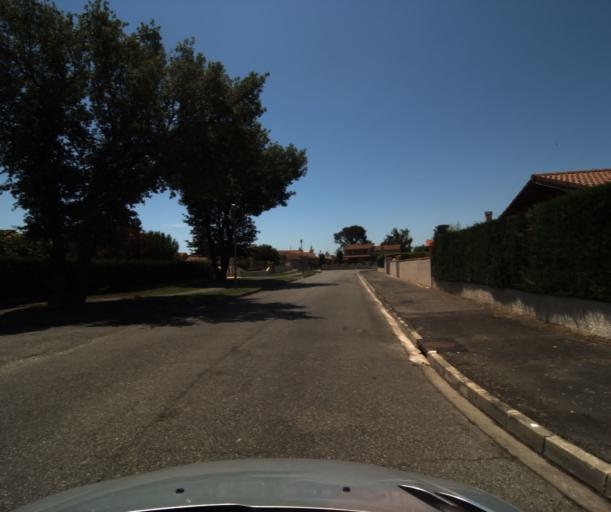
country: FR
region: Midi-Pyrenees
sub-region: Departement de la Haute-Garonne
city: Roquettes
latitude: 43.4917
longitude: 1.3791
